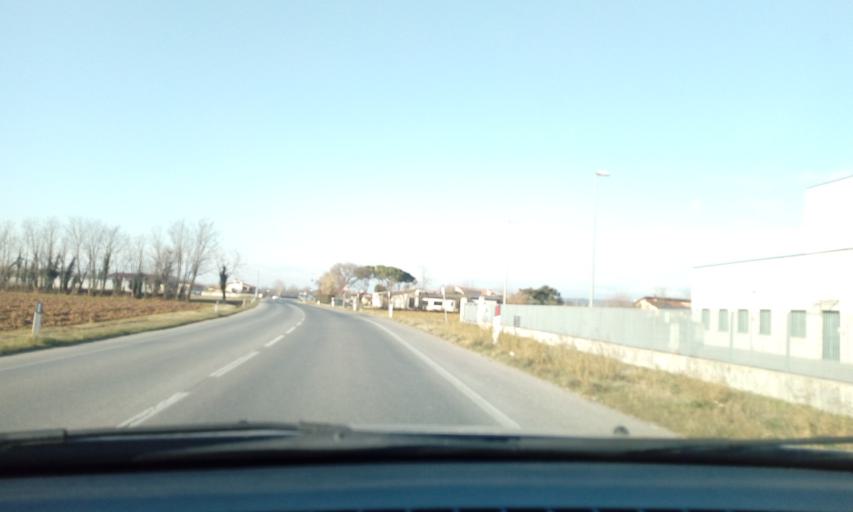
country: IT
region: Friuli Venezia Giulia
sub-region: Provincia di Gorizia
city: Romans d'Isonzo
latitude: 45.8836
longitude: 13.4348
